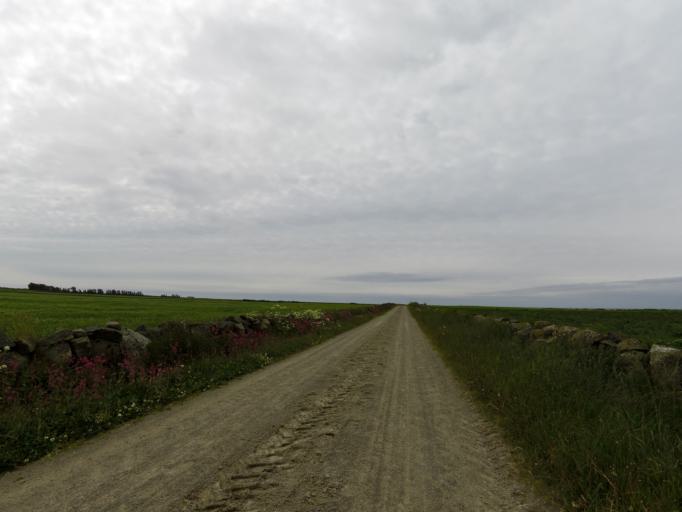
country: NO
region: Rogaland
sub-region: Ha
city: Naerbo
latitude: 58.6771
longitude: 5.5530
